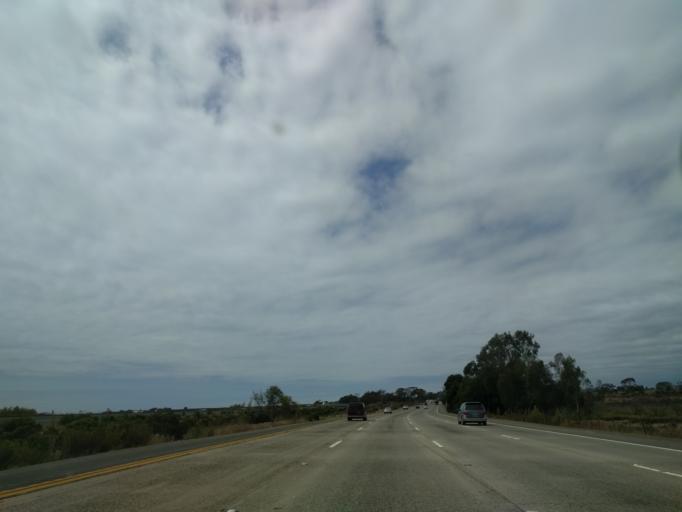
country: US
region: California
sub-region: San Diego County
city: Camp Pendleton South
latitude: 33.2317
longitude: -117.4014
